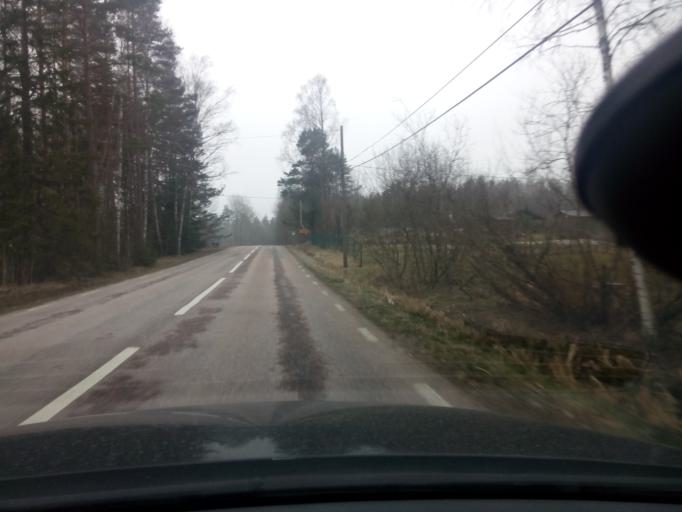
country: SE
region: Soedermanland
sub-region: Nykopings Kommun
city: Nykoping
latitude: 58.9328
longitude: 17.1112
